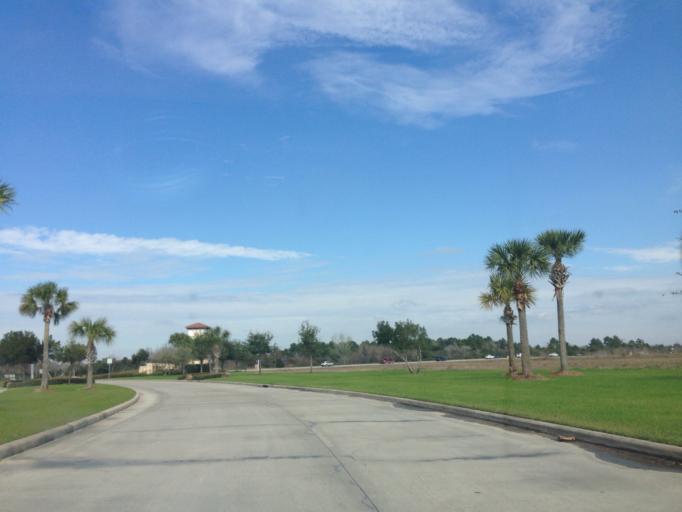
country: US
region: Texas
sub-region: Galveston County
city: Kemah
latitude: 29.5174
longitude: -95.0220
